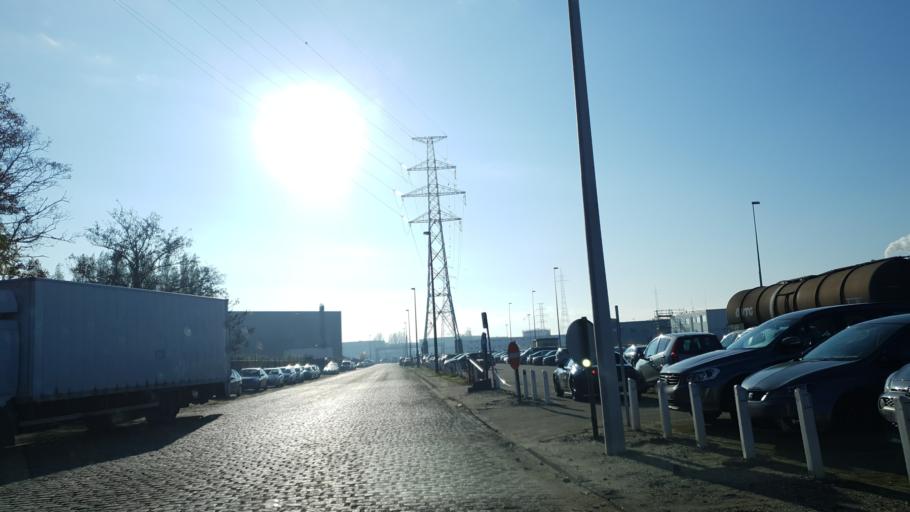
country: BE
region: Flanders
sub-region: Provincie Antwerpen
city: Zwijndrecht
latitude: 51.2594
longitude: 4.3475
